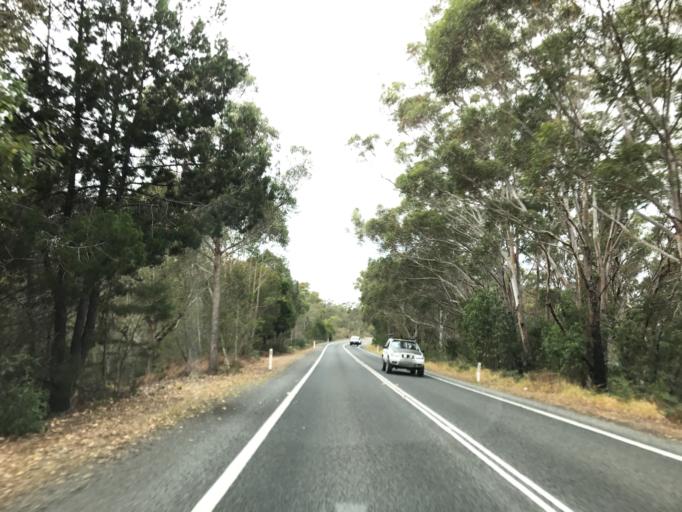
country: AU
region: Queensland
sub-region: Redland
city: Victoria Point
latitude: -27.4342
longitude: 153.4684
